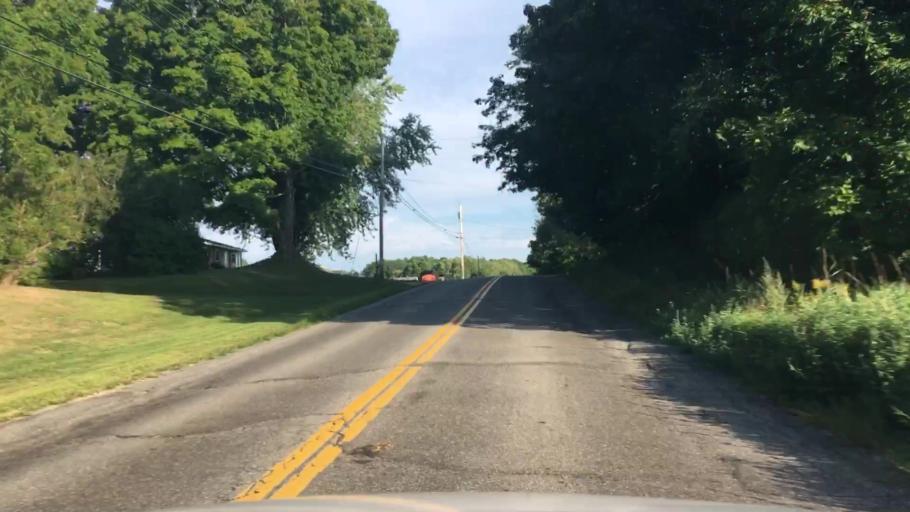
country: US
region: Maine
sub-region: Cumberland County
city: South Windham
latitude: 43.7213
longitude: -70.3992
